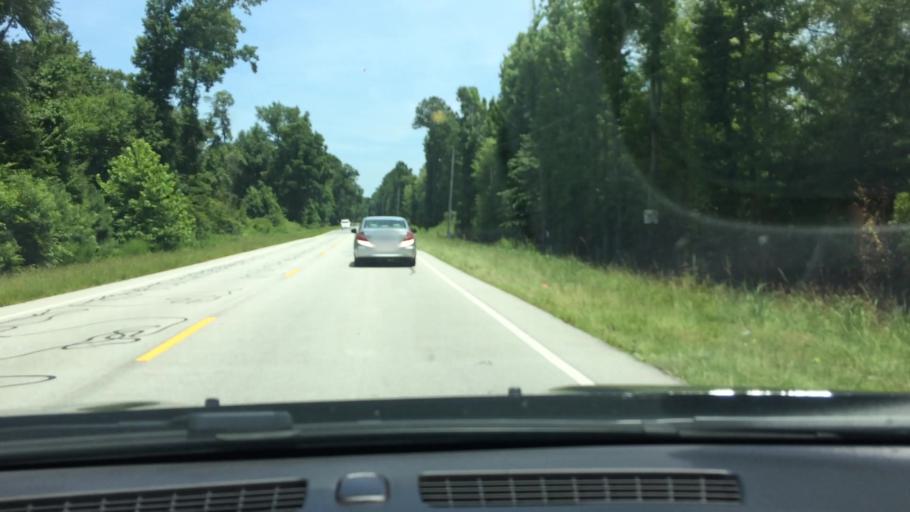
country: US
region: North Carolina
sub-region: Beaufort County
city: Washington
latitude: 35.5803
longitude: -77.1710
